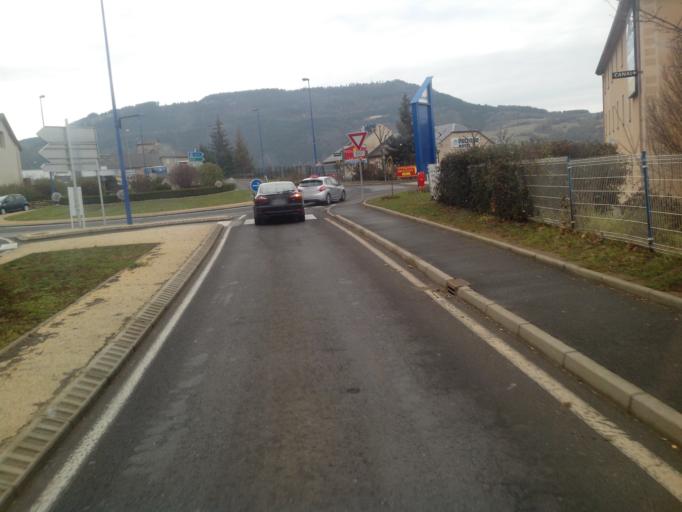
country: FR
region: Languedoc-Roussillon
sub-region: Departement de la Lozere
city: Mende
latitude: 44.5163
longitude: 3.4859
